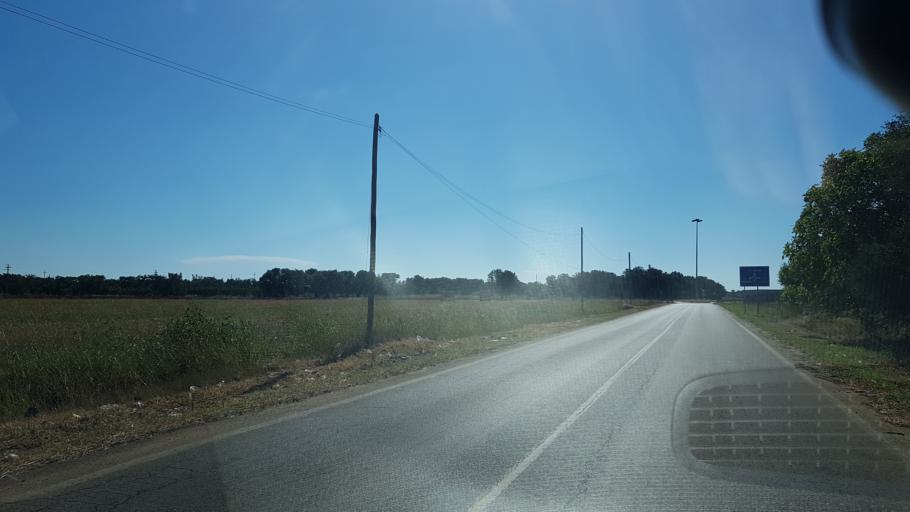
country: IT
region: Apulia
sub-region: Provincia di Brindisi
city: Mesagne
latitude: 40.5574
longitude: 17.8397
